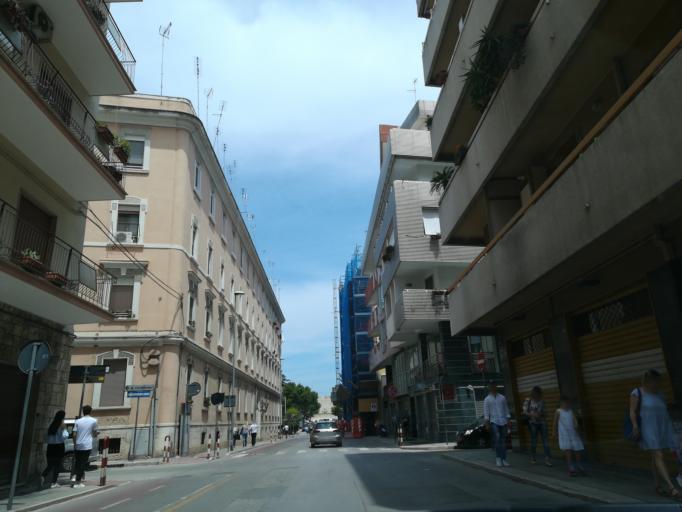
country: IT
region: Apulia
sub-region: Provincia di Barletta - Andria - Trani
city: Barletta
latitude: 41.3182
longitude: 16.2873
